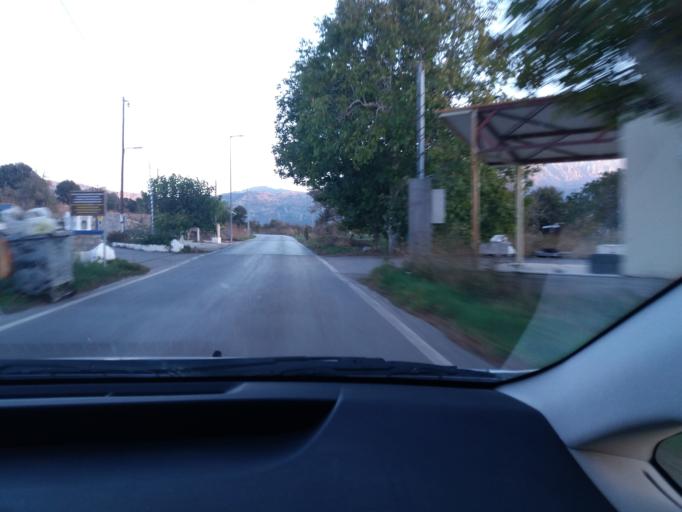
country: GR
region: Crete
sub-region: Nomos Irakleiou
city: Malia
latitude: 35.1932
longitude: 25.4903
